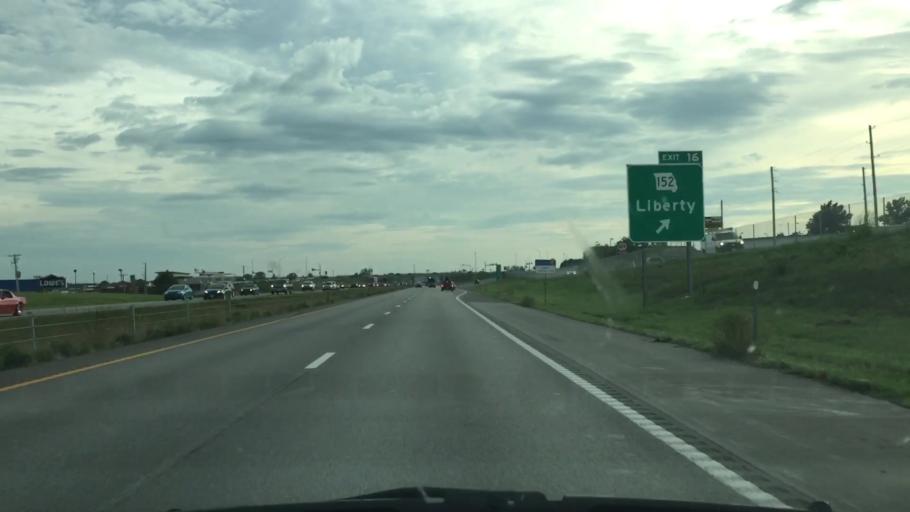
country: US
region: Missouri
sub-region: Clay County
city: Liberty
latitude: 39.2490
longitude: -94.4523
